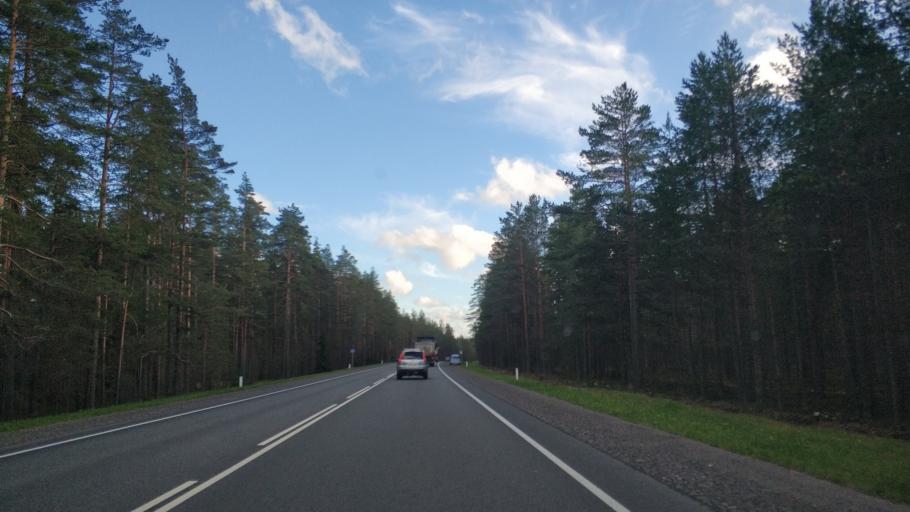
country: RU
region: Leningrad
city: Priozersk
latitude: 60.8874
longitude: 30.1604
